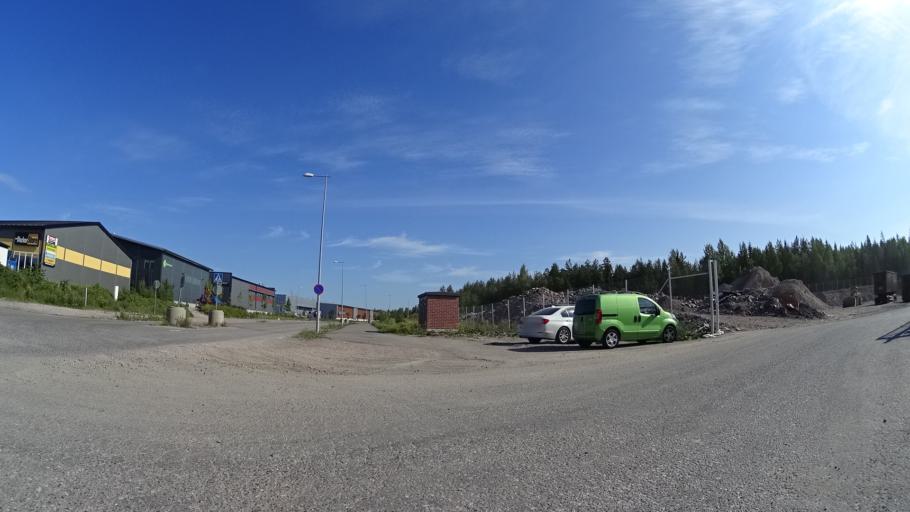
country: FI
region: Uusimaa
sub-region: Helsinki
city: Kilo
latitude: 60.2903
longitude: 24.7664
